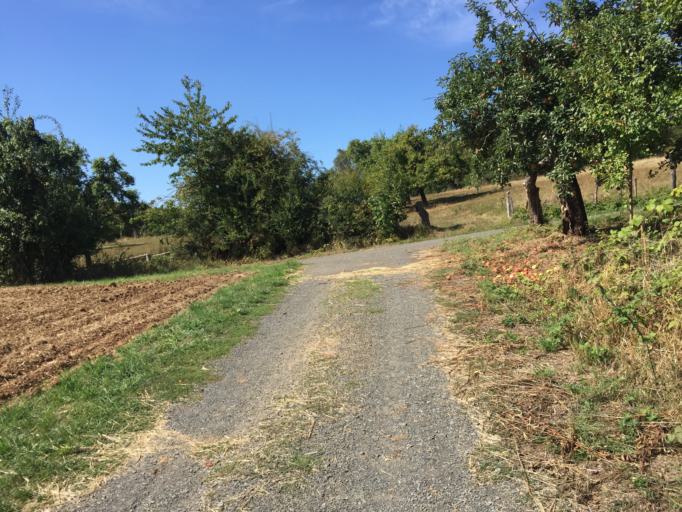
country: DE
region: Hesse
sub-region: Regierungsbezirk Giessen
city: Reiskirchen
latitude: 50.6016
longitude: 8.8866
